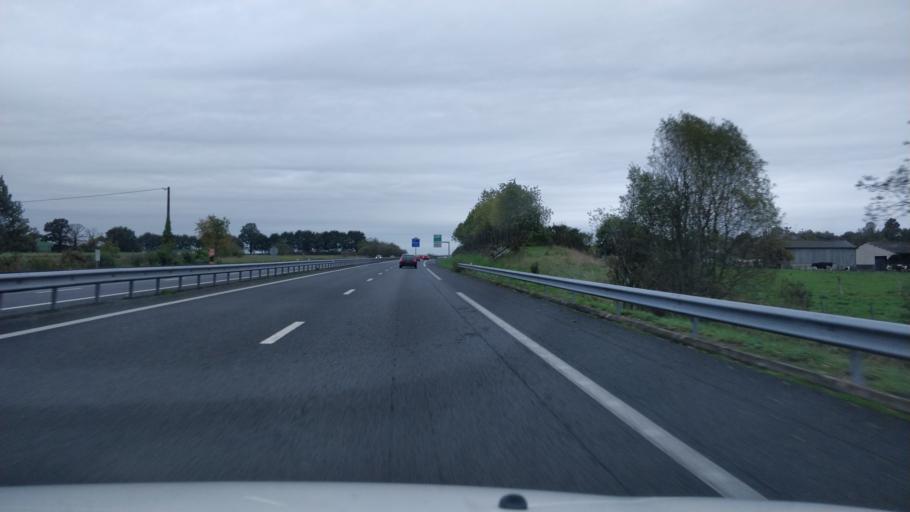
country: FR
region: Brittany
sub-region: Departement d'Ille-et-Vilaine
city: Saint-Etienne-en-Cogles
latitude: 48.3904
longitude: -1.3070
